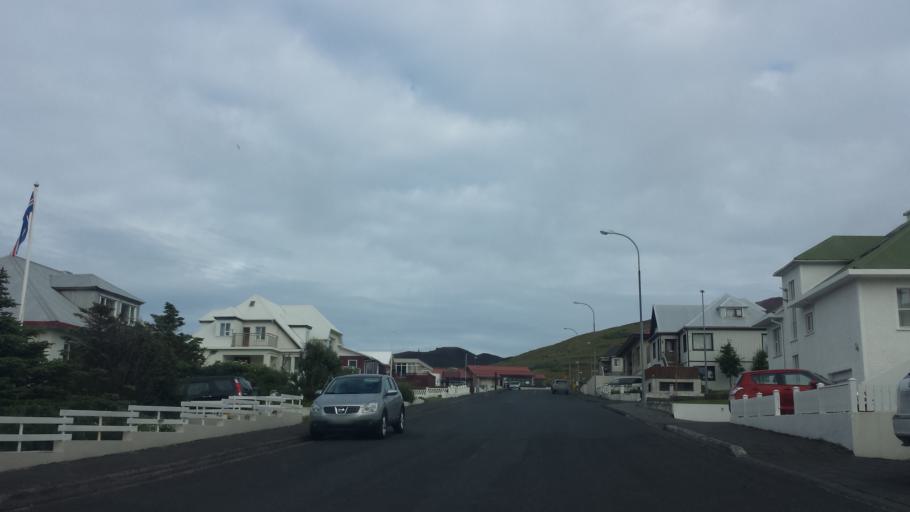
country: IS
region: South
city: Vestmannaeyjar
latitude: 63.4378
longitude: -20.2663
